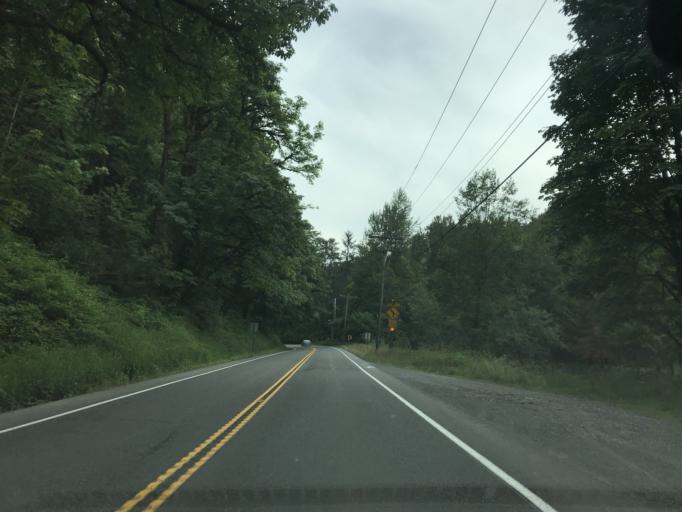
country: US
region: Washington
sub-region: King County
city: Fall City
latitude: 47.5556
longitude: -121.8989
